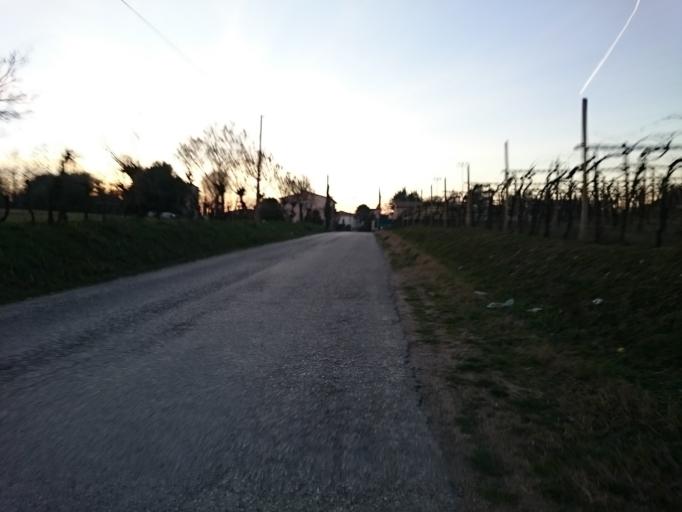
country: IT
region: Veneto
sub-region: Provincia di Verona
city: Salionze
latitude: 45.4067
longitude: 10.7547
